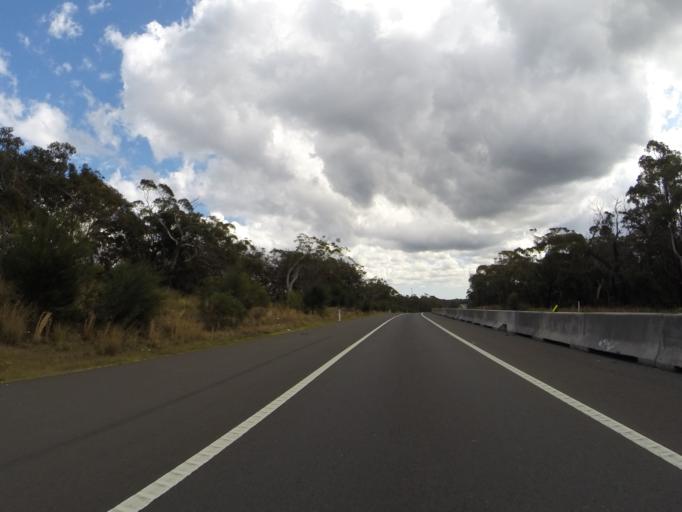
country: AU
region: New South Wales
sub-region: Wollongong
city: Mount Keira
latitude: -34.3324
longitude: 150.7793
